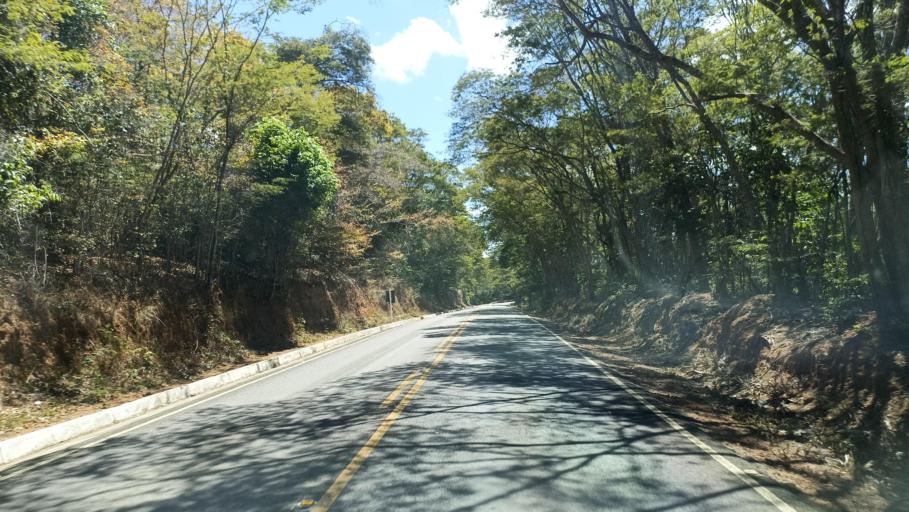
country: BR
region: Bahia
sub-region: Andarai
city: Vera Cruz
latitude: -12.7719
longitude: -41.3306
